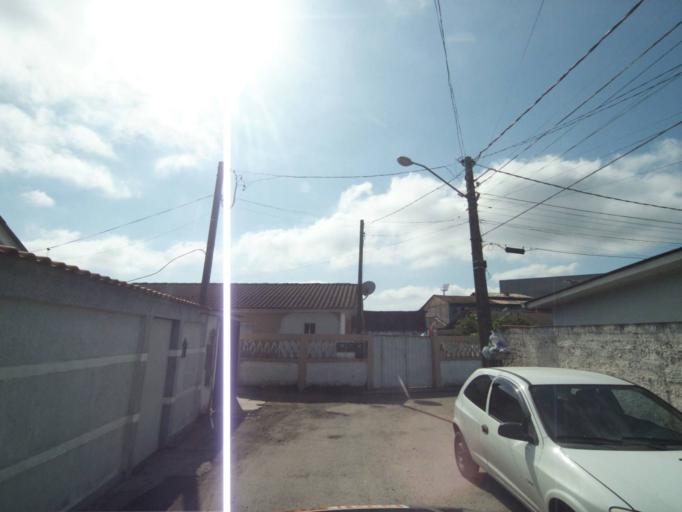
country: BR
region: Parana
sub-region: Paranagua
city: Paranagua
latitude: -25.5255
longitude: -48.5107
